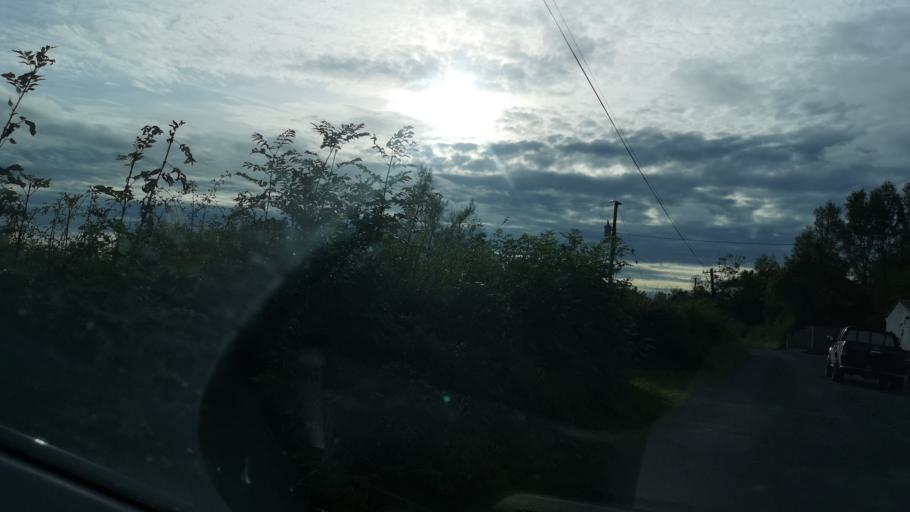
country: IE
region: Connaught
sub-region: County Galway
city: Ballinasloe
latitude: 53.3430
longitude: -8.2860
